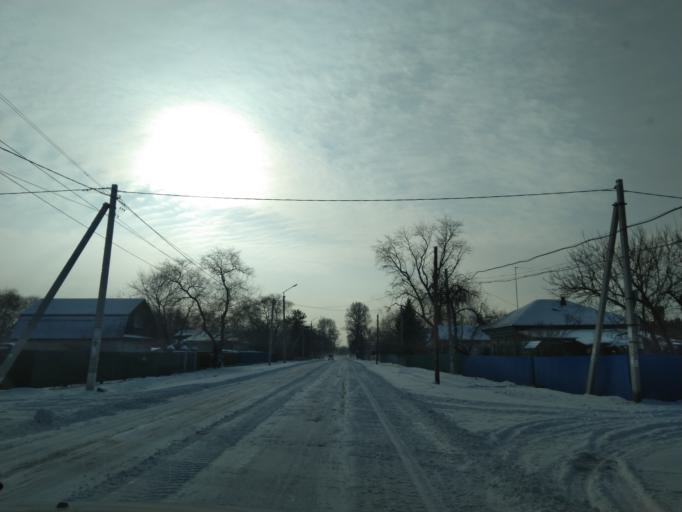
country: RU
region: Amur
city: Poyarkovo
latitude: 49.6274
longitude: 128.6500
